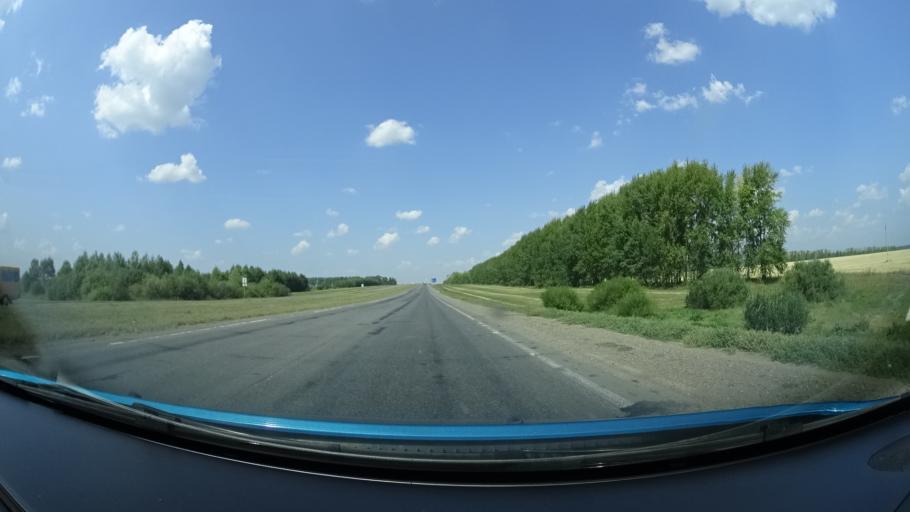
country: RU
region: Bashkortostan
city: Chishmy
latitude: 54.6647
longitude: 55.4259
